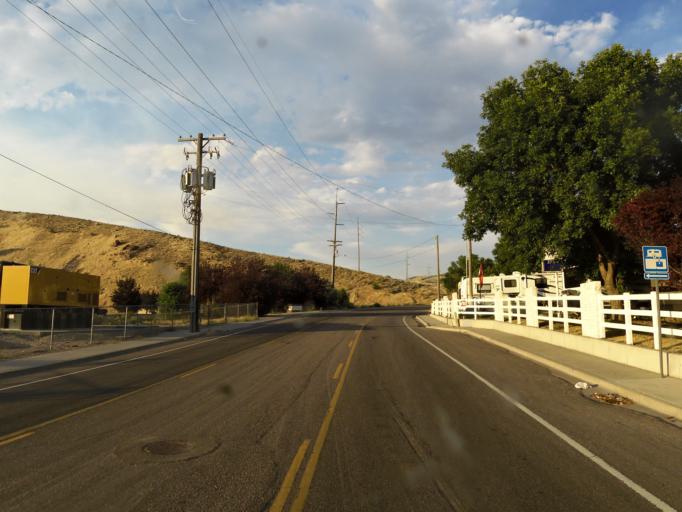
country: US
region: Idaho
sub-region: Bannock County
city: Pocatello
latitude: 42.8501
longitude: -112.4209
